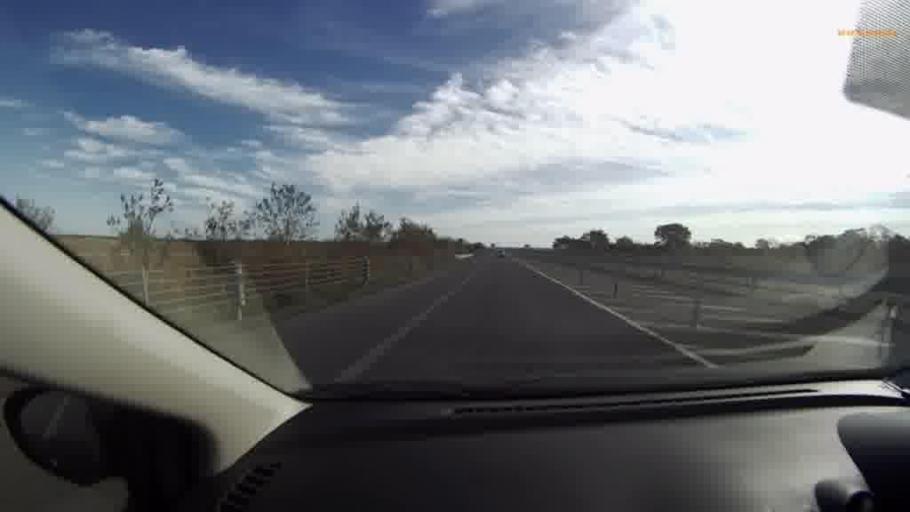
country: JP
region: Hokkaido
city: Kushiro
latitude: 43.0373
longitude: 144.3394
